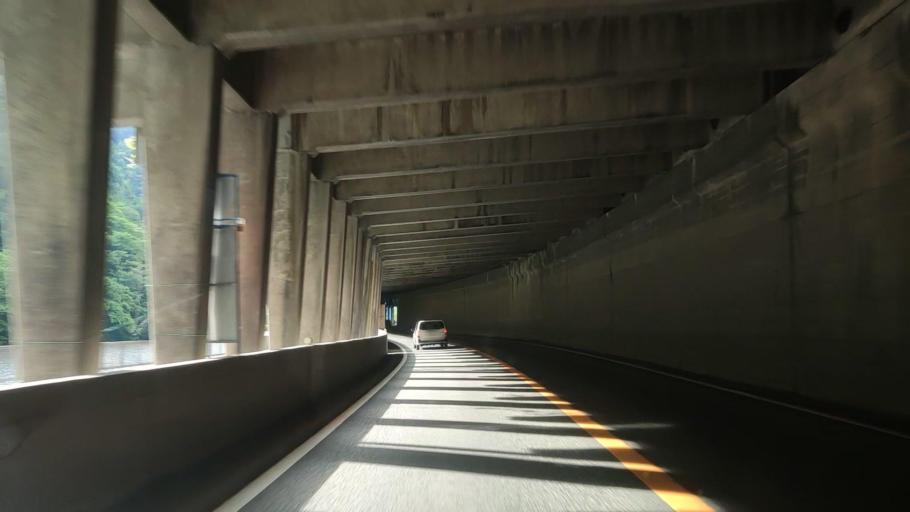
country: JP
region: Toyama
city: Yatsuomachi-higashikumisaka
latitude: 36.4164
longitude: 137.2895
